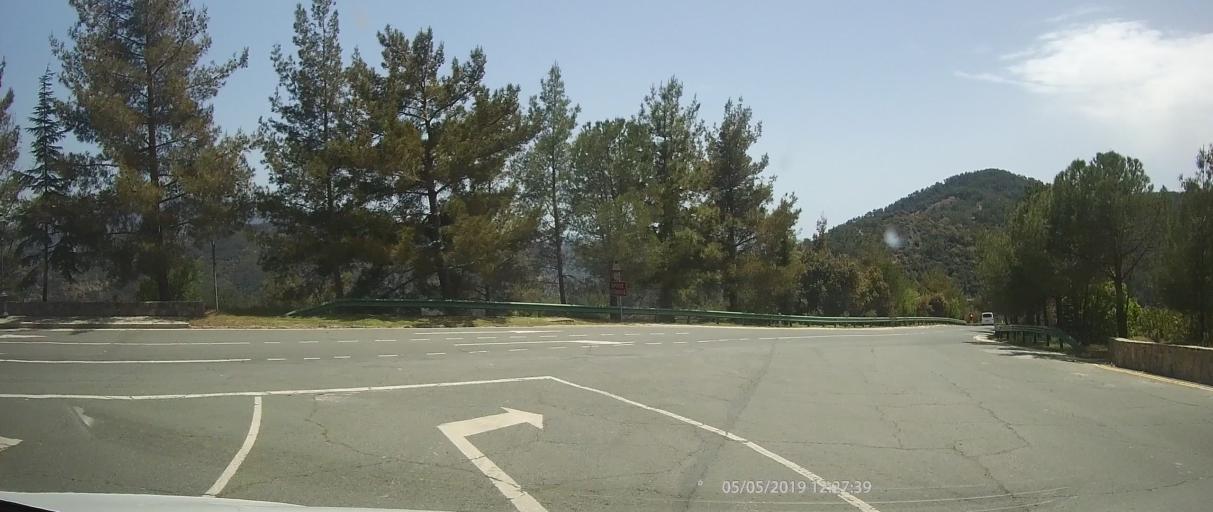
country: CY
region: Lefkosia
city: Kakopetria
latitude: 34.9820
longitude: 32.7421
